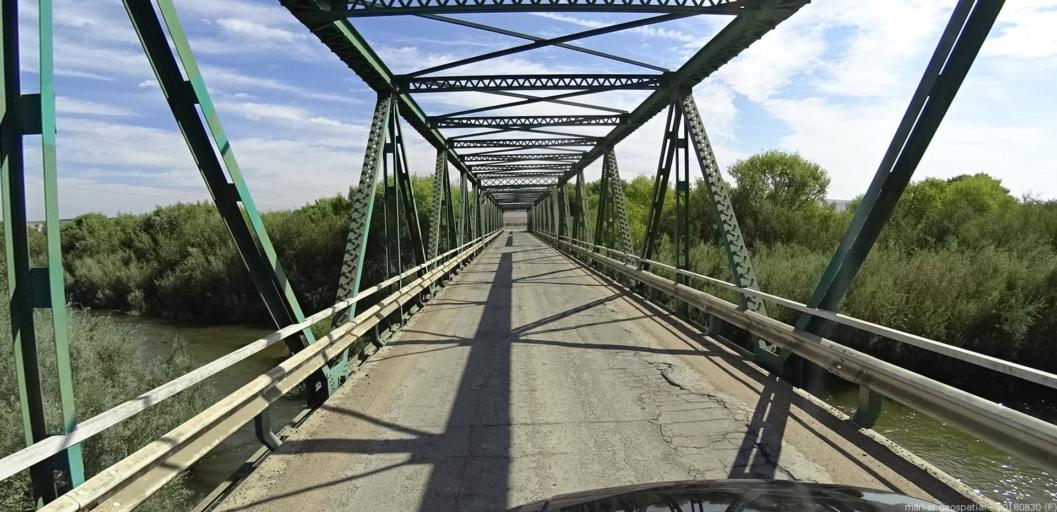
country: US
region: California
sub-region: Monterey County
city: King City
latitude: 36.1169
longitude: -121.0281
